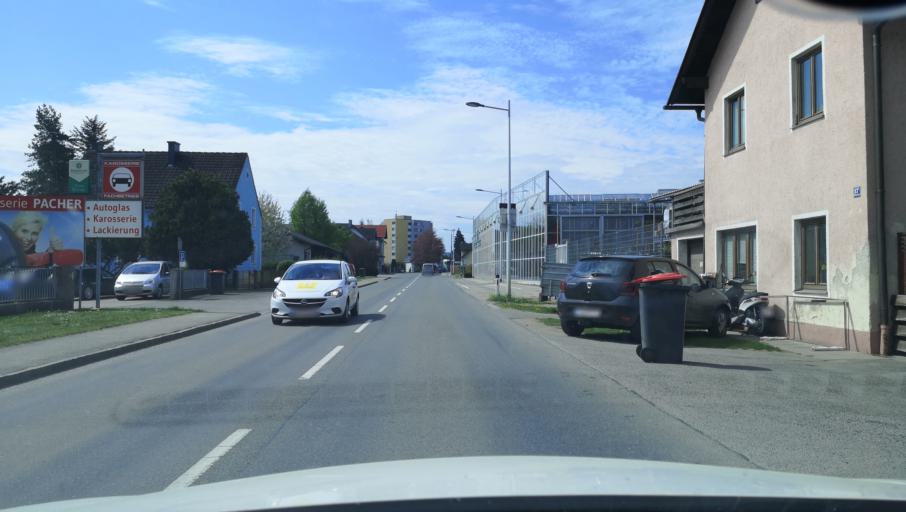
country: AT
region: Lower Austria
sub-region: Politischer Bezirk Melk
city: Petzenkirchen
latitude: 48.1357
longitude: 15.1429
